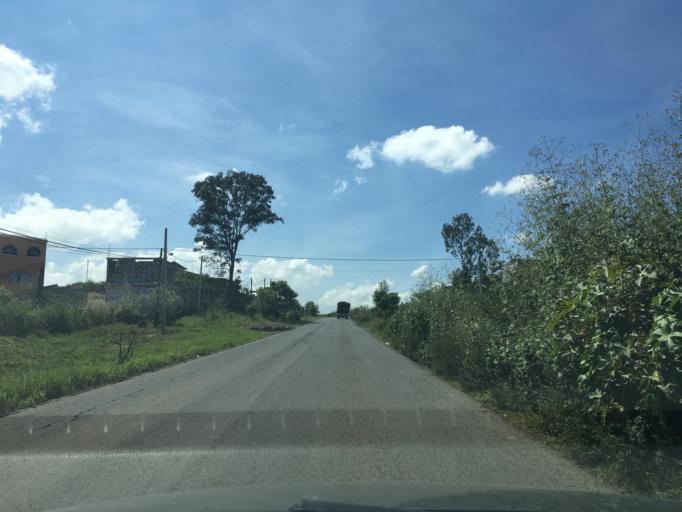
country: MX
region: Michoacan
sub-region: Morelia
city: San Antonio
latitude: 19.6680
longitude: -101.2823
